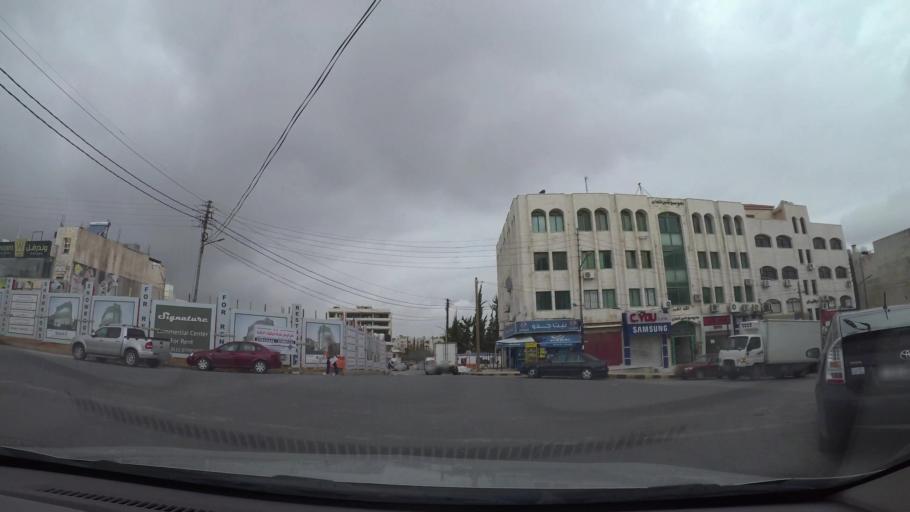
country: JO
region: Amman
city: Wadi as Sir
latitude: 31.9747
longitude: 35.8515
